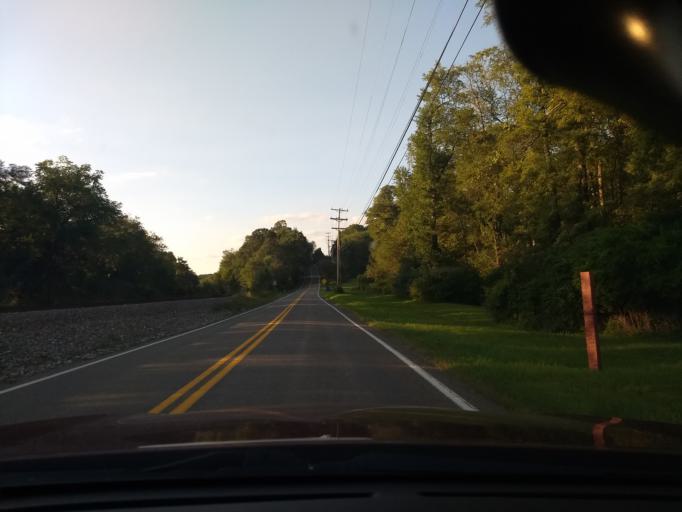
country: US
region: Pennsylvania
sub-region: Allegheny County
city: Gibsonia
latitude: 40.6428
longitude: -79.9702
